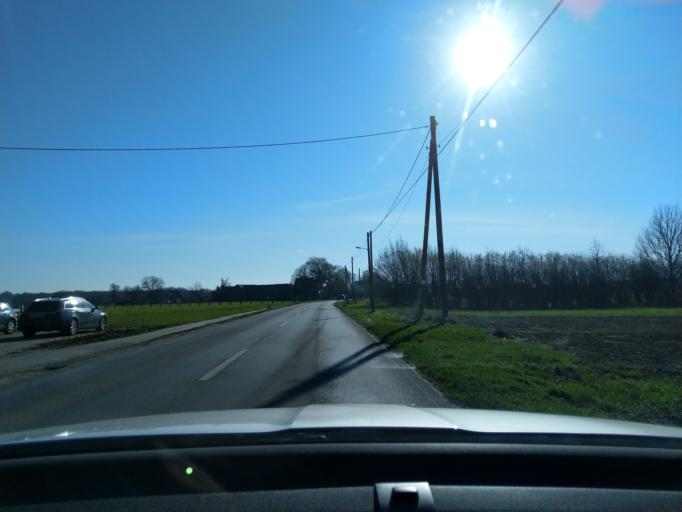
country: DE
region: North Rhine-Westphalia
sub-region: Regierungsbezirk Dusseldorf
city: Monchengladbach
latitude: 51.1410
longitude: 6.3740
